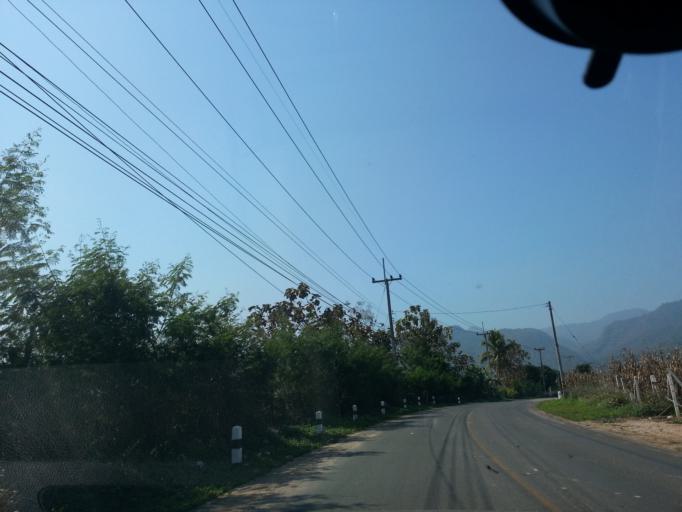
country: TH
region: Chiang Mai
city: Chai Prakan
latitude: 19.8078
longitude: 99.1243
